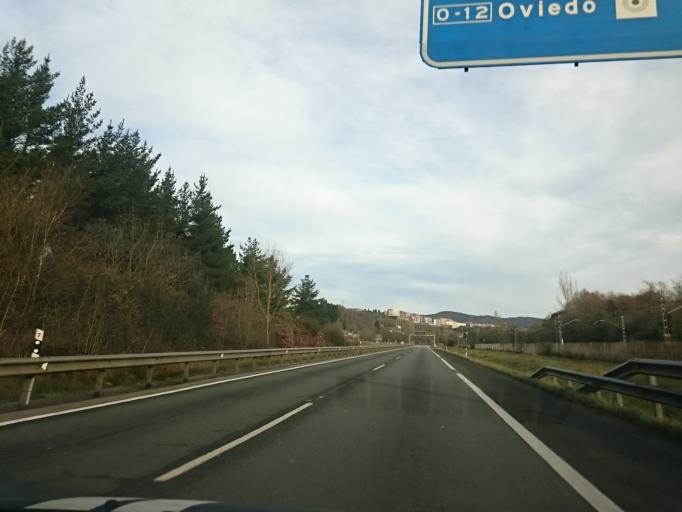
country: ES
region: Asturias
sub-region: Province of Asturias
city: Oviedo
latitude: 43.3343
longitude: -5.8700
